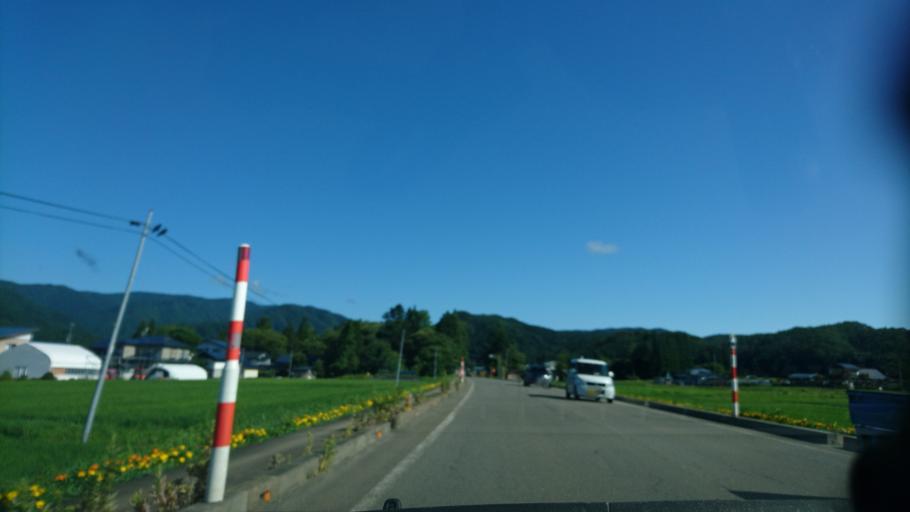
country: JP
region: Akita
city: Kakunodatemachi
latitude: 39.6664
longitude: 140.5687
